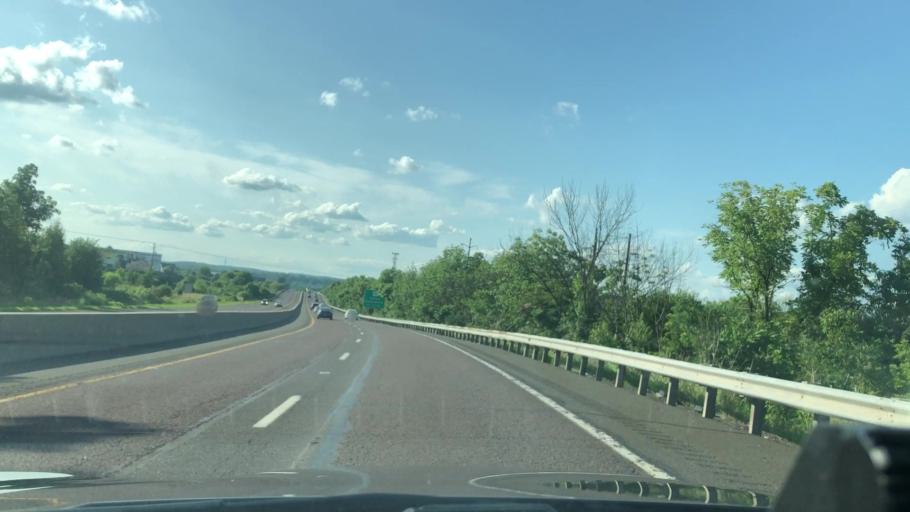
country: US
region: Pennsylvania
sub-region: Bucks County
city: Sellersville
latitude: 40.3341
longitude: -75.3103
